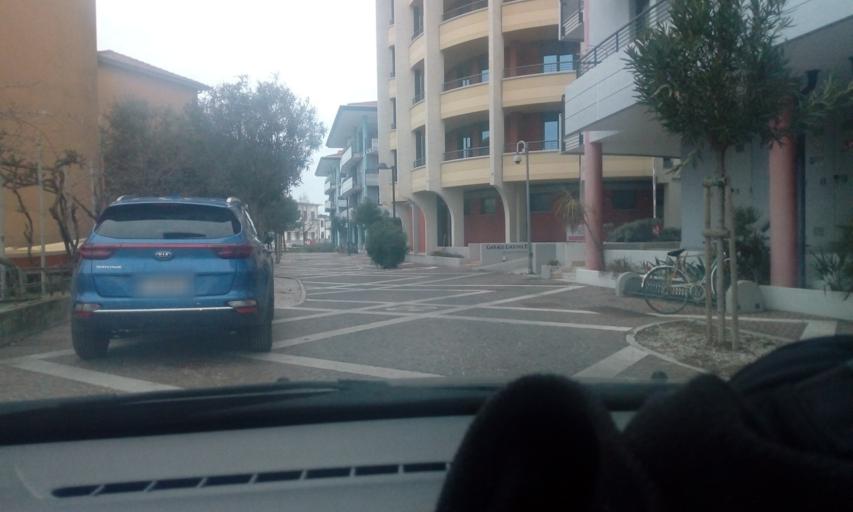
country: IT
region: Friuli Venezia Giulia
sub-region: Provincia di Gorizia
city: Grado
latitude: 45.6822
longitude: 13.3798
